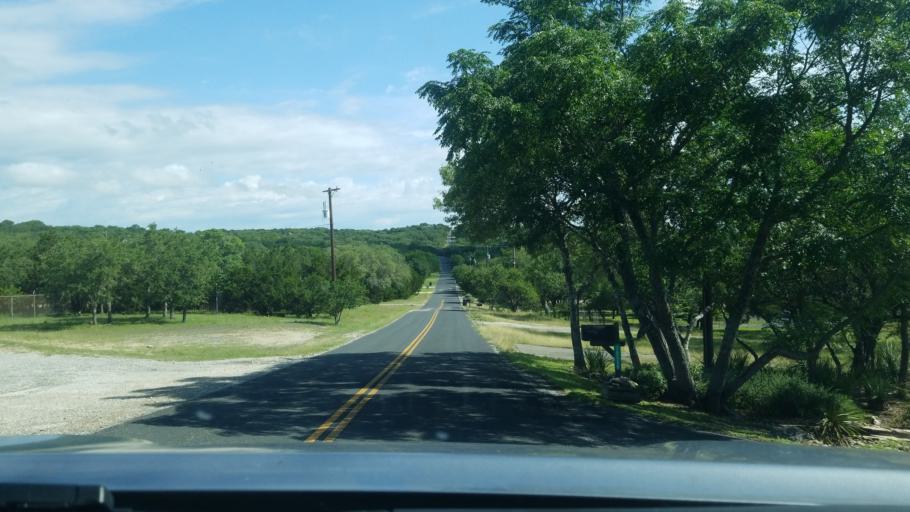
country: US
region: Texas
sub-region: Comal County
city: Bulverde
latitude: 29.7488
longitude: -98.4427
